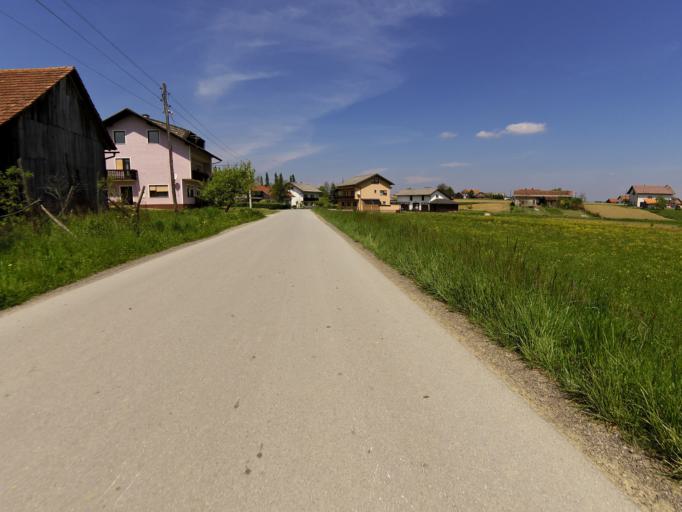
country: HR
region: Karlovacka
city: Ozalj
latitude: 45.5613
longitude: 15.4794
